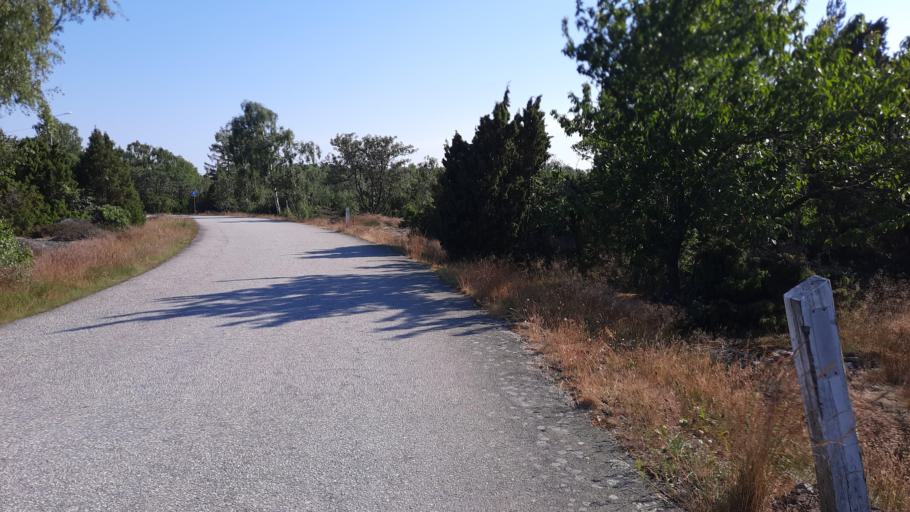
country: SE
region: Blekinge
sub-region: Karlskrona Kommun
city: Sturko
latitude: 56.1207
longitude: 15.6586
